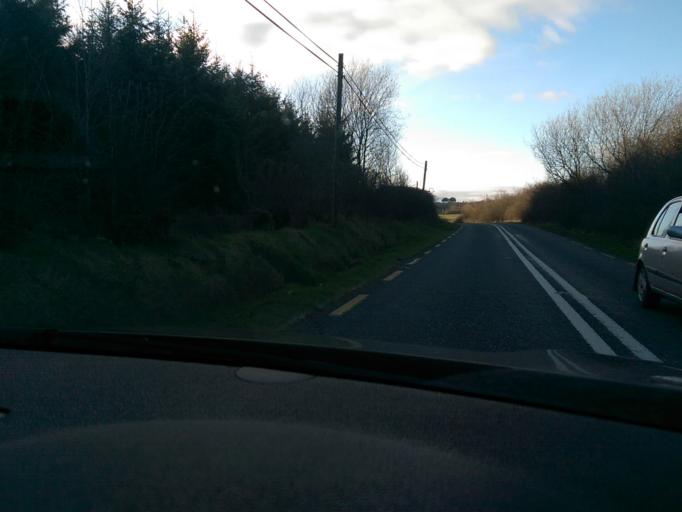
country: IE
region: Connaught
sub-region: Roscommon
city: Boyle
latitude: 53.9099
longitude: -8.2673
